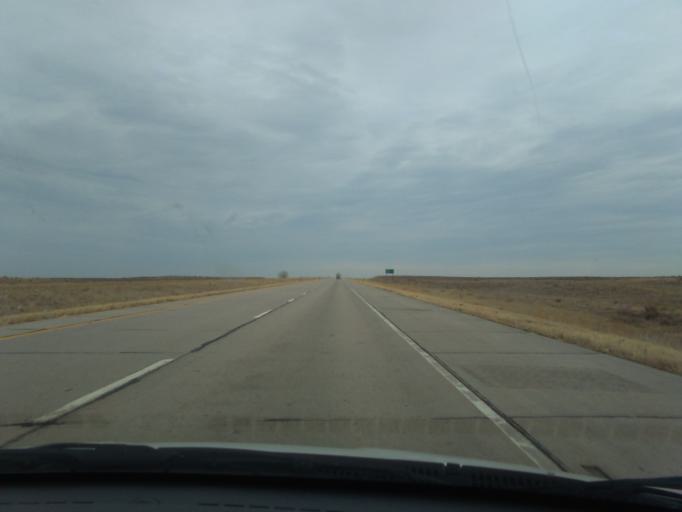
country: US
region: Colorado
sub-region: Weld County
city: Keenesburg
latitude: 40.1866
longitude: -104.2982
